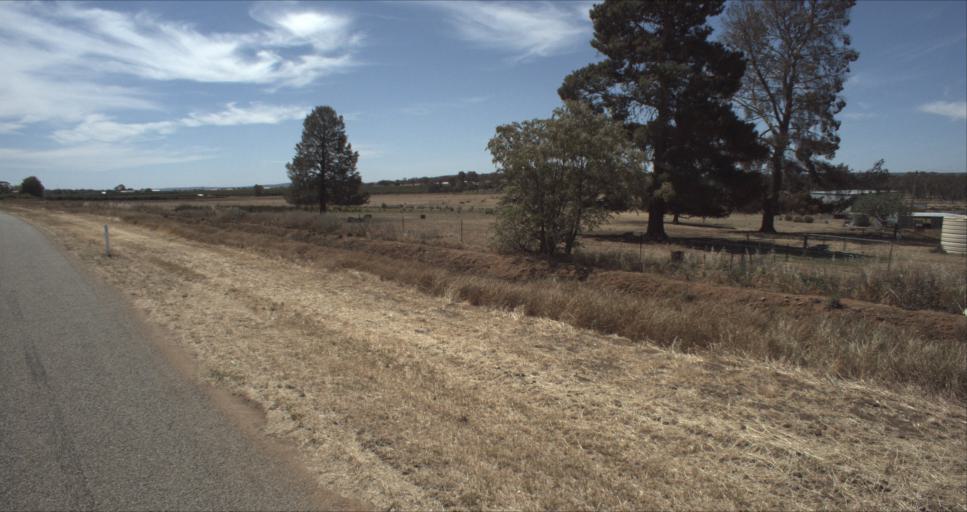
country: AU
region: New South Wales
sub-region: Leeton
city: Leeton
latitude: -34.5974
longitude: 146.4779
